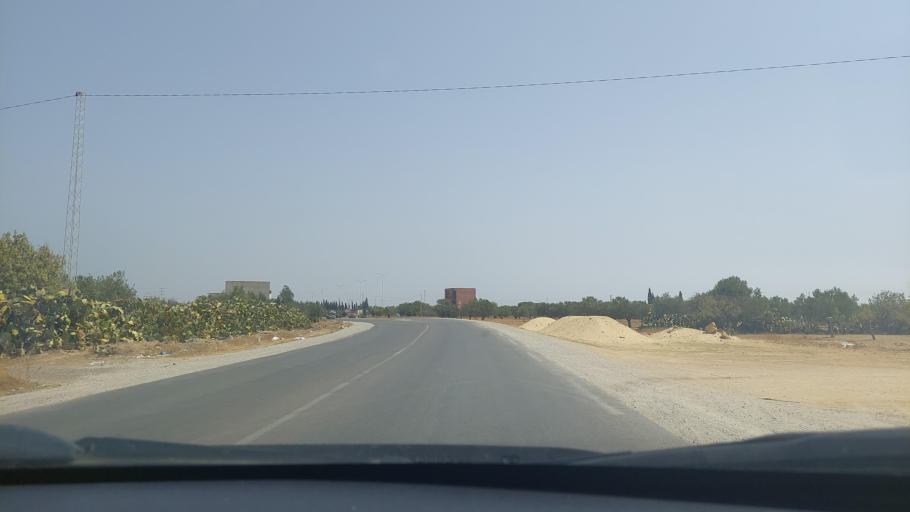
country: TN
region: Al Munastir
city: Qasr Hallal
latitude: 35.6024
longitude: 10.8958
